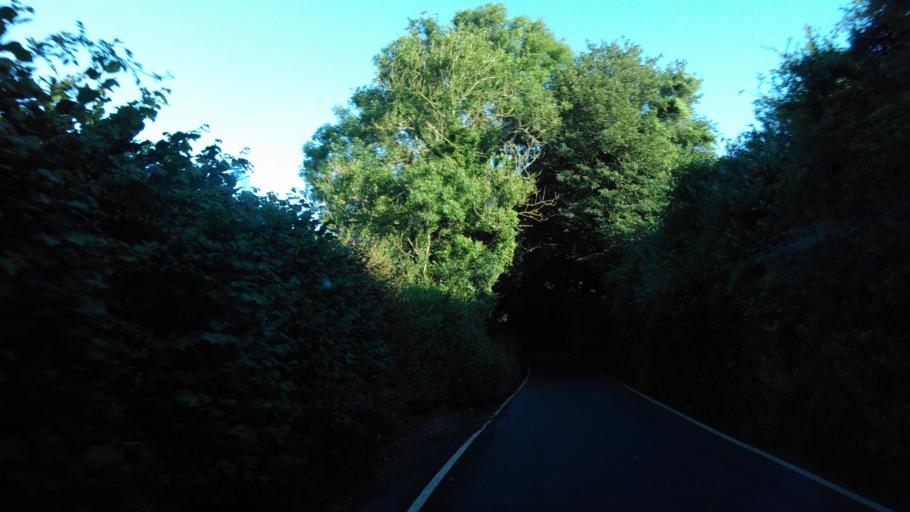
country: GB
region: England
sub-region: Kent
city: Chartham
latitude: 51.2644
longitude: 1.0141
